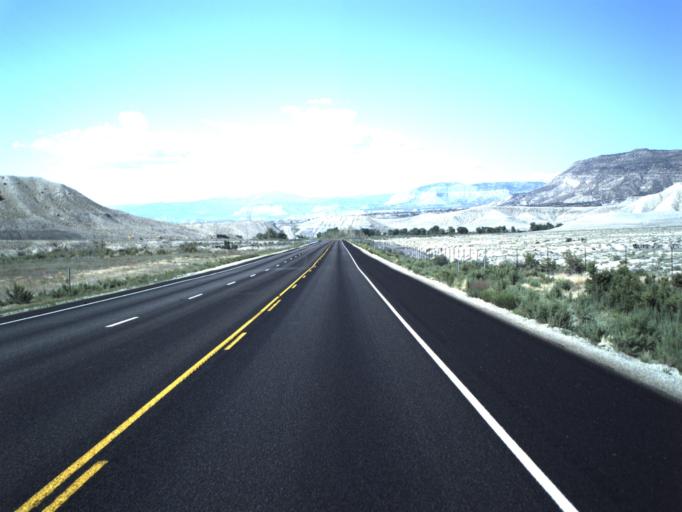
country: US
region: Utah
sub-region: Emery County
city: Ferron
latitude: 38.9624
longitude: -111.1946
